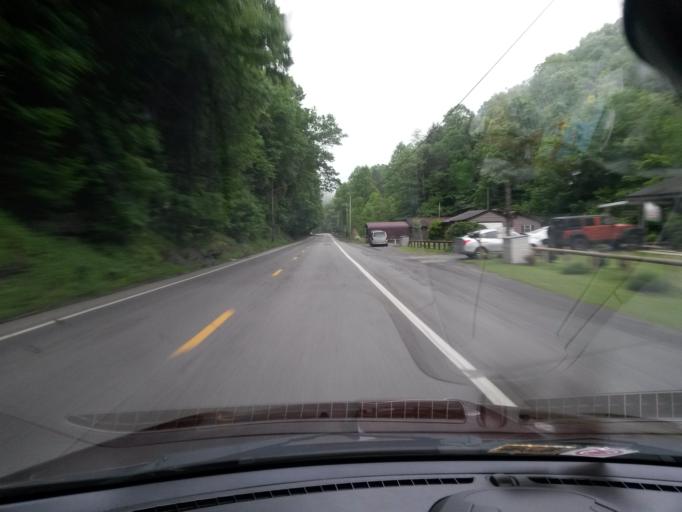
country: US
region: West Virginia
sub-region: Wyoming County
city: Pineville
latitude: 37.5432
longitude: -81.5831
